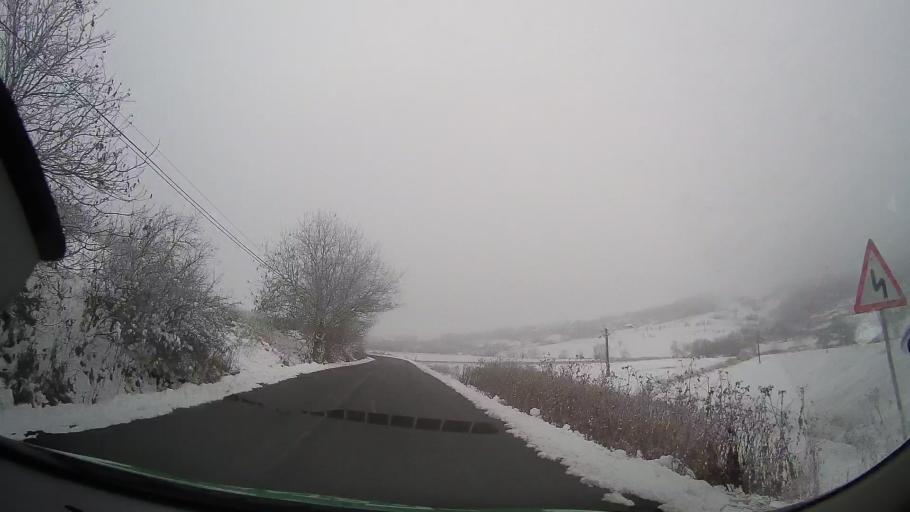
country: RO
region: Bacau
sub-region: Comuna Oncesti
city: Oncesti
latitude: 46.4790
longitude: 27.2578
